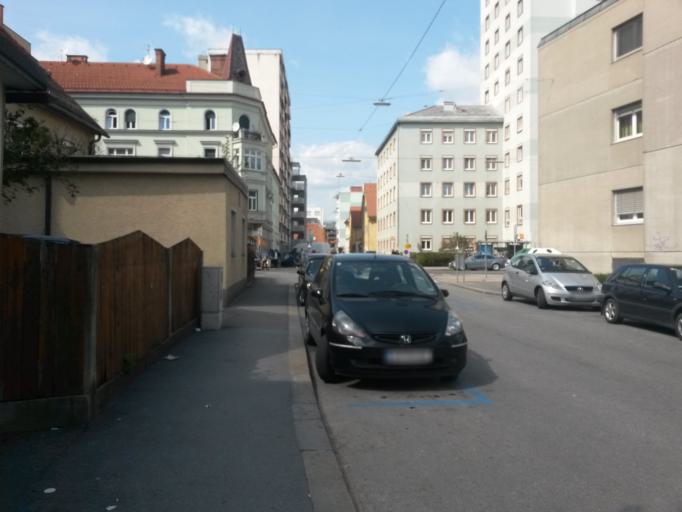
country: AT
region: Styria
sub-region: Graz Stadt
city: Graz
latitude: 47.0756
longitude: 15.4287
